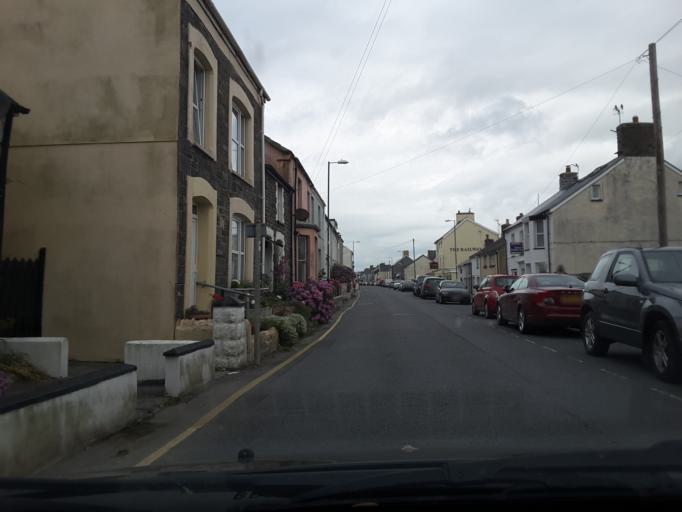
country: GB
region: Wales
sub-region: County of Ceredigion
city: Bow Street
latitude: 52.4855
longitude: -4.0510
